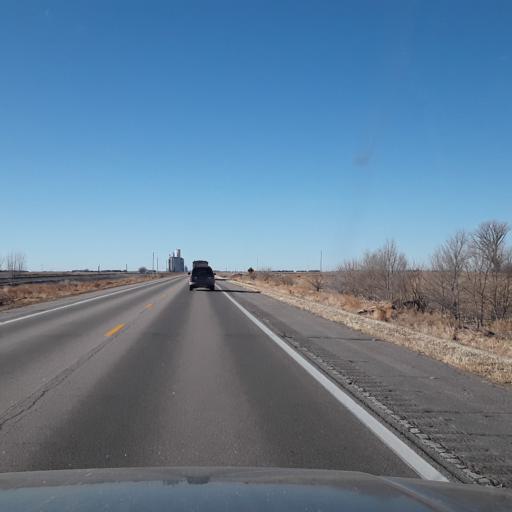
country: US
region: Nebraska
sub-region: Kearney County
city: Minden
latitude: 40.4952
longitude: -99.0054
